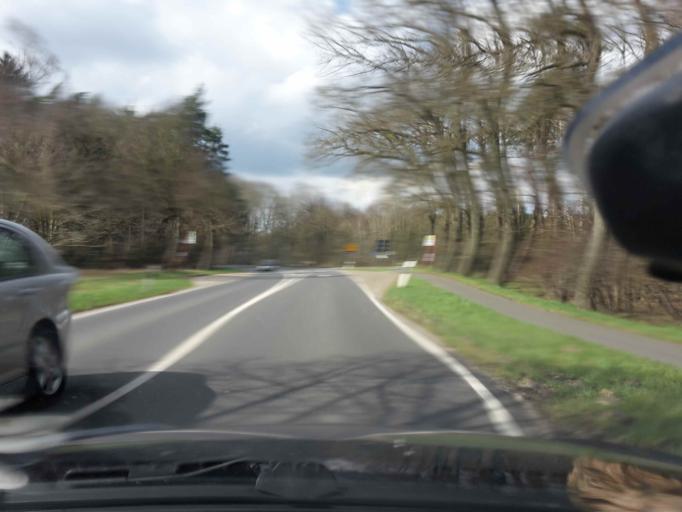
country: DE
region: Lower Saxony
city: Asendorf
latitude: 53.2866
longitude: 10.0014
